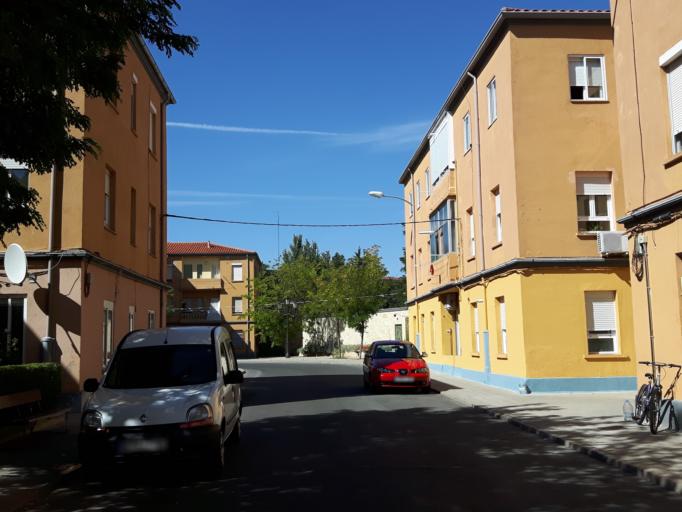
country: ES
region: Castille and Leon
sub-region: Provincia de Salamanca
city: Salamanca
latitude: 40.9818
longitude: -5.6592
